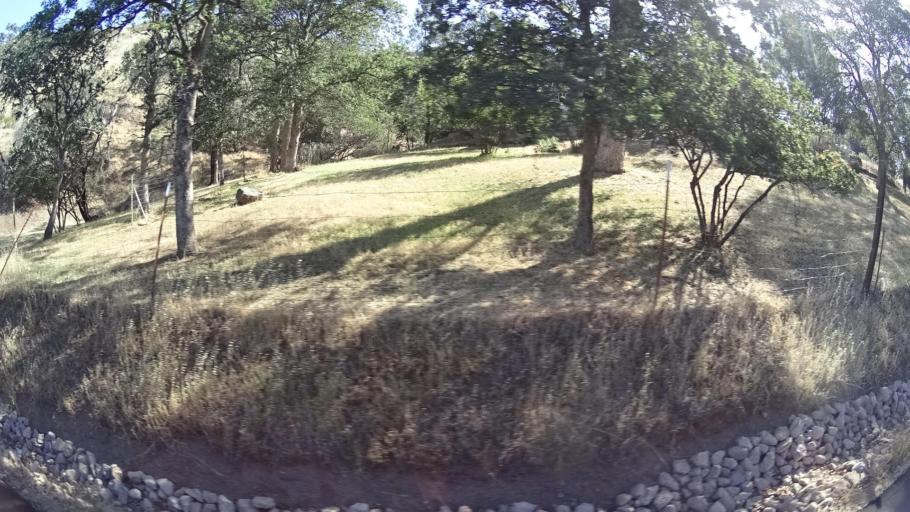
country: US
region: California
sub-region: Lake County
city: Clearlake Oaks
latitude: 38.9816
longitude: -122.6884
